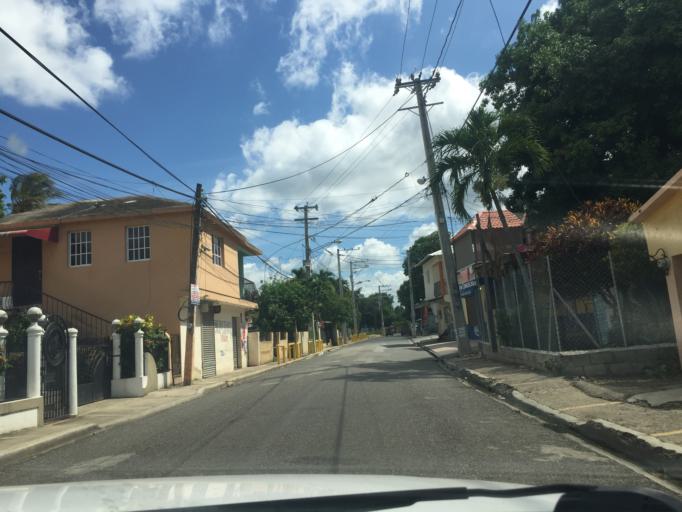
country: DO
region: Santiago
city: Licey al Medio
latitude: 19.3834
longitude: -70.6041
